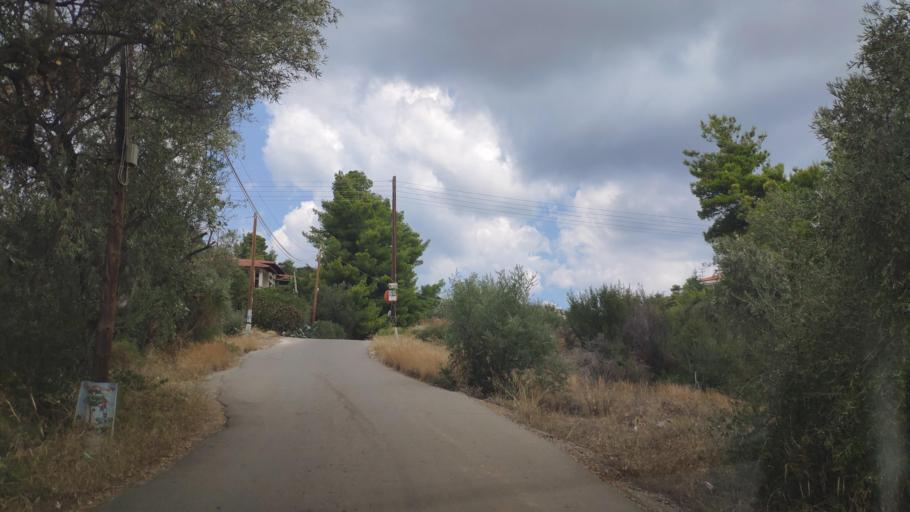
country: GR
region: Central Greece
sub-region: Nomos Fthiotidos
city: Malesina
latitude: 38.6652
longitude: 23.1816
